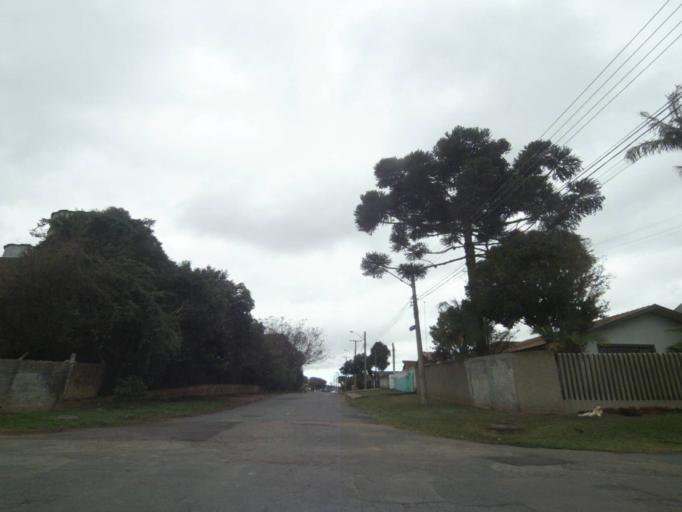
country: BR
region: Parana
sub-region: Sao Jose Dos Pinhais
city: Sao Jose dos Pinhais
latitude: -25.5392
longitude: -49.2986
